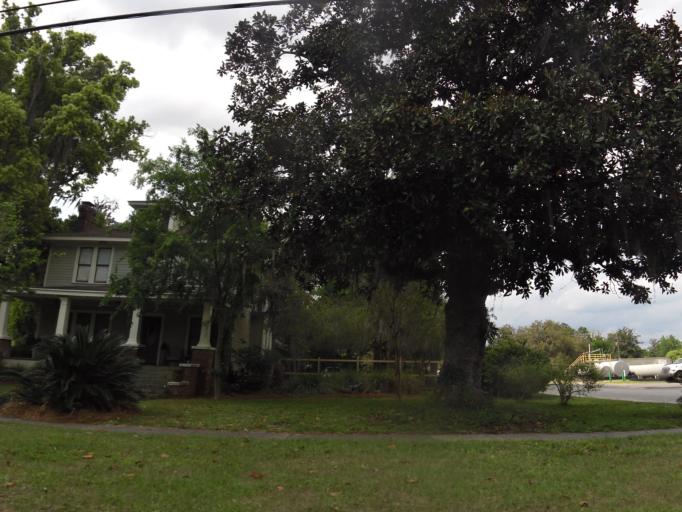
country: US
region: Georgia
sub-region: Charlton County
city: Folkston
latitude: 30.8306
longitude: -82.0110
